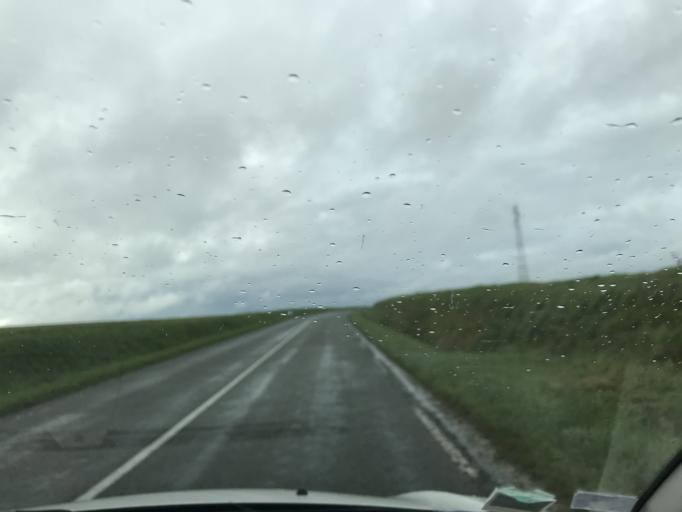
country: FR
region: Picardie
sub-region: Departement de l'Aisne
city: Billy-sur-Aisne
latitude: 49.3500
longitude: 3.3634
